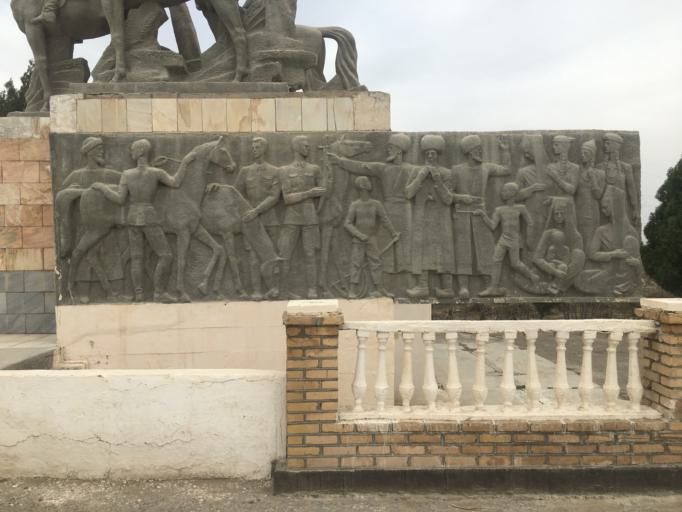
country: TM
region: Mary
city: Bayramaly
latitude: 37.5553
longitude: 62.2064
